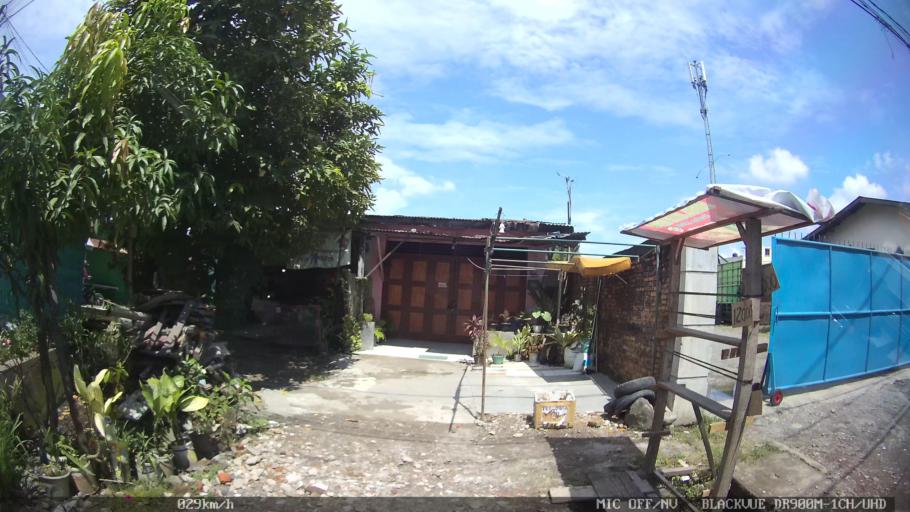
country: ID
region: North Sumatra
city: Medan
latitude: 3.5981
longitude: 98.7465
